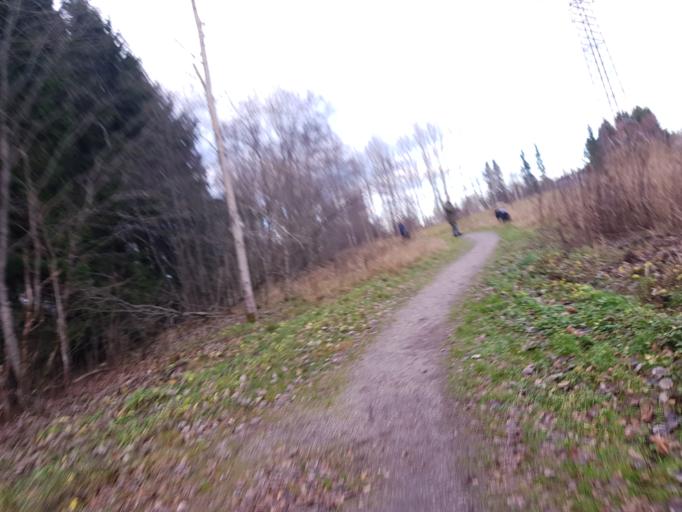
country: FI
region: Uusimaa
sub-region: Helsinki
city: Helsinki
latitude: 60.2720
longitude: 24.9095
